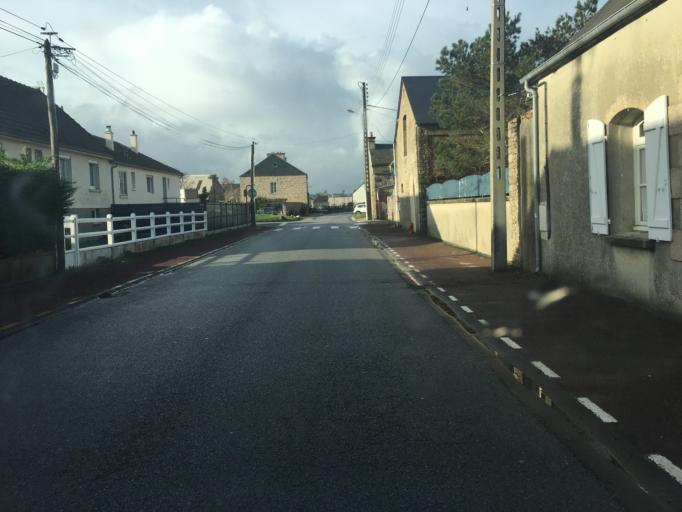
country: FR
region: Lower Normandy
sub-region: Departement de la Manche
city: Saint-Vaast-la-Hougue
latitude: 49.5856
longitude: -1.2697
